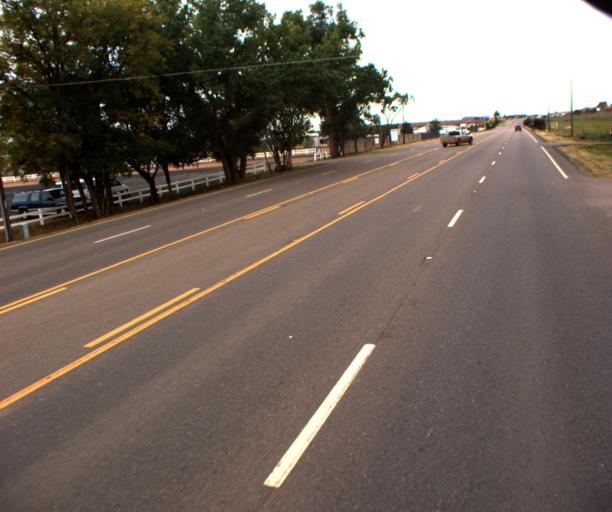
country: US
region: Arizona
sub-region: Navajo County
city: Taylor
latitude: 34.4867
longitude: -110.0828
